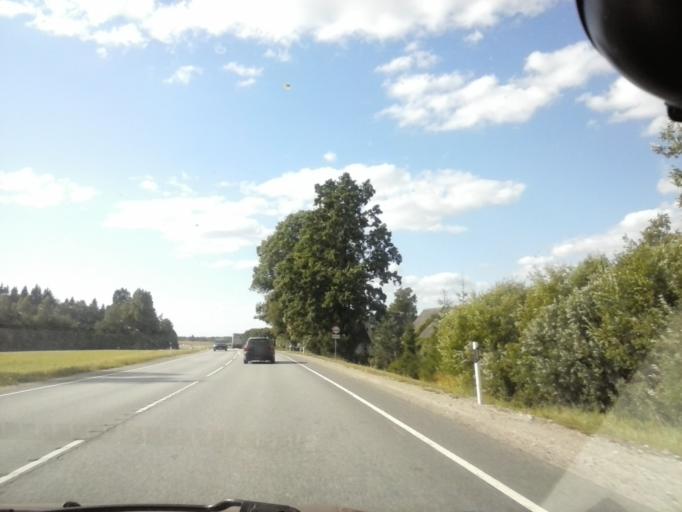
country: EE
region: Jogevamaa
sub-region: Poltsamaa linn
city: Poltsamaa
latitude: 58.6284
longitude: 26.1496
